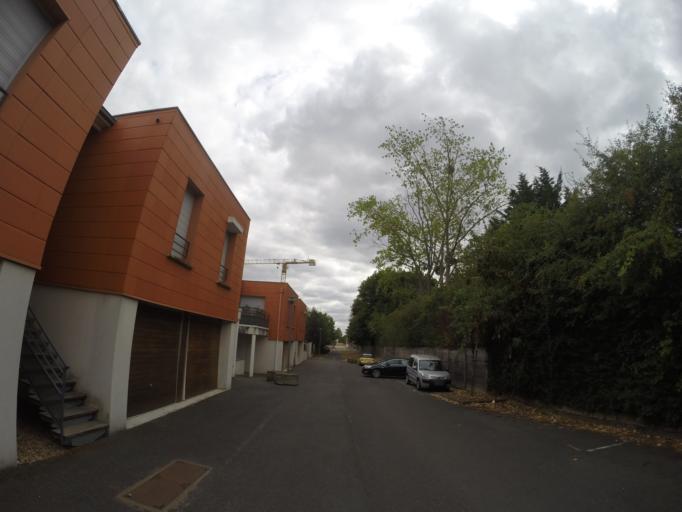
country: FR
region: Centre
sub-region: Departement d'Indre-et-Loire
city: Saint-Cyr-sur-Loire
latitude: 47.4198
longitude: 0.7010
